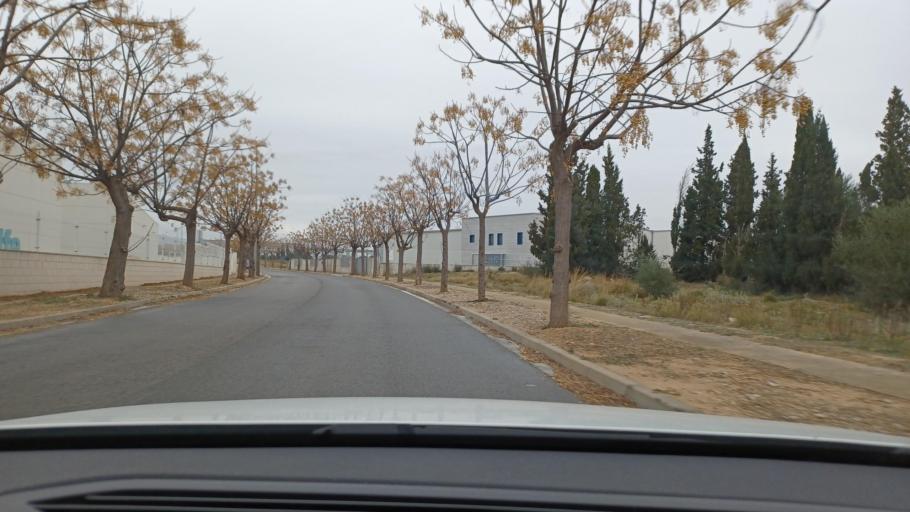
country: ES
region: Catalonia
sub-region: Provincia de Tarragona
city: Amposta
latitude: 40.7562
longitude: 0.6005
